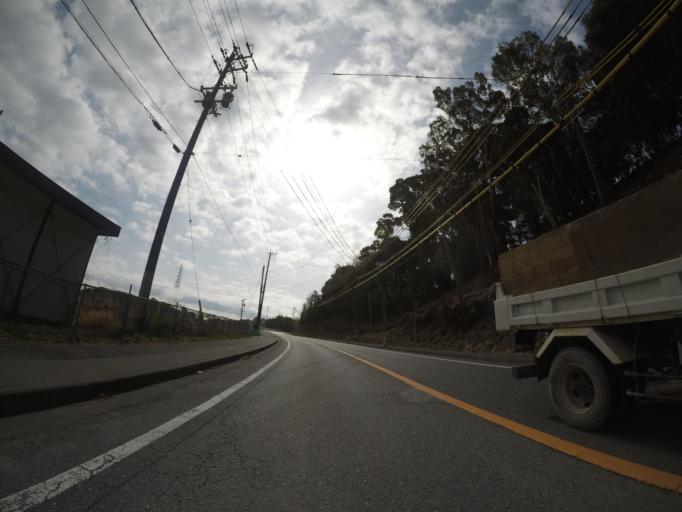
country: JP
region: Shizuoka
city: Hamakita
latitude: 34.8035
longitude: 137.6945
